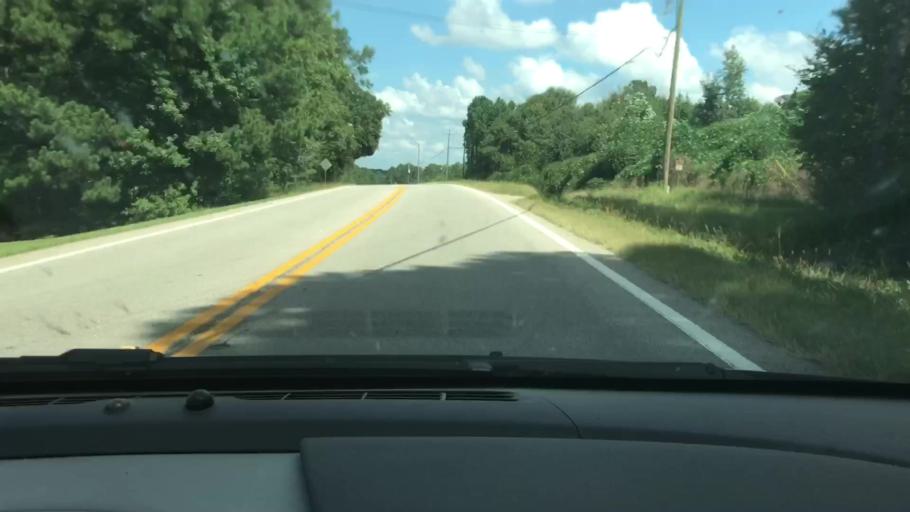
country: US
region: Georgia
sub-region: Troup County
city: La Grange
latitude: 32.9518
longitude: -85.0182
